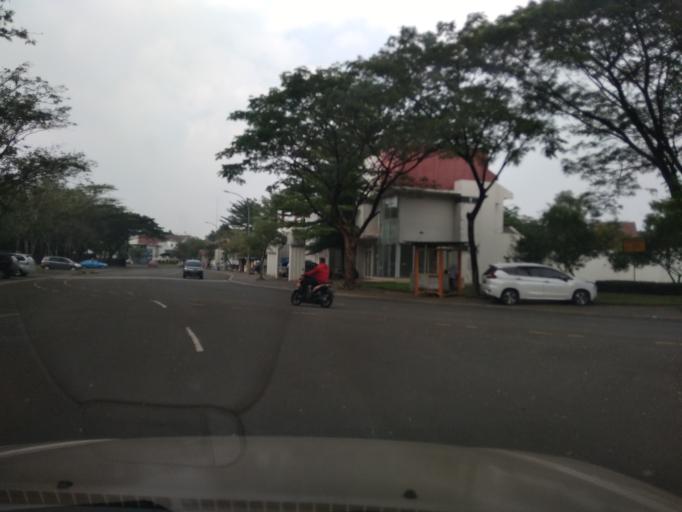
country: ID
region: West Java
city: Serpong
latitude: -6.3147
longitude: 106.6448
